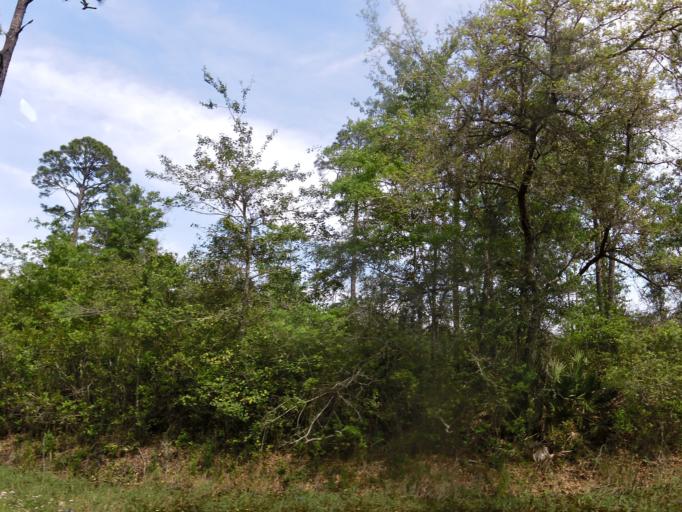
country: US
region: Georgia
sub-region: Camden County
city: Kingsland
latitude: 30.7648
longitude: -81.6597
